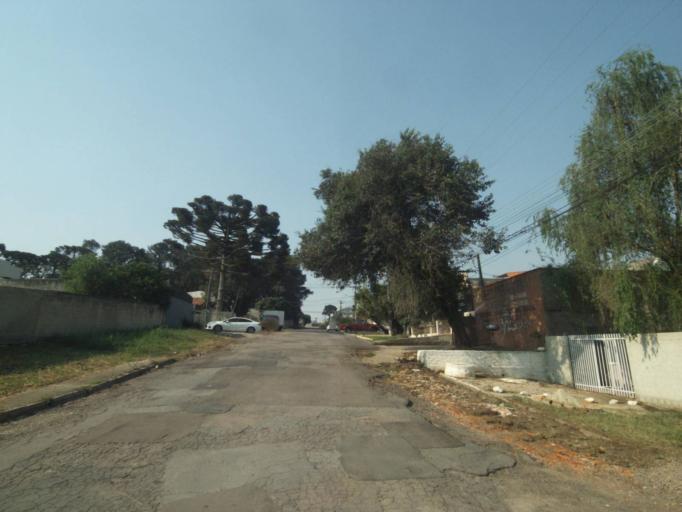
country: BR
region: Parana
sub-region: Curitiba
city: Curitiba
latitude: -25.5012
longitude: -49.2780
